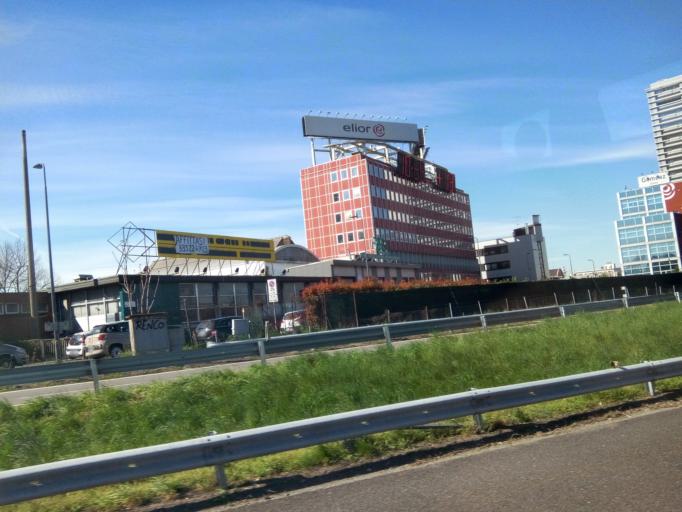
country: IT
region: Lombardy
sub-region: Citta metropolitana di Milano
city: Baranzate
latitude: 45.5151
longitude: 9.1186
